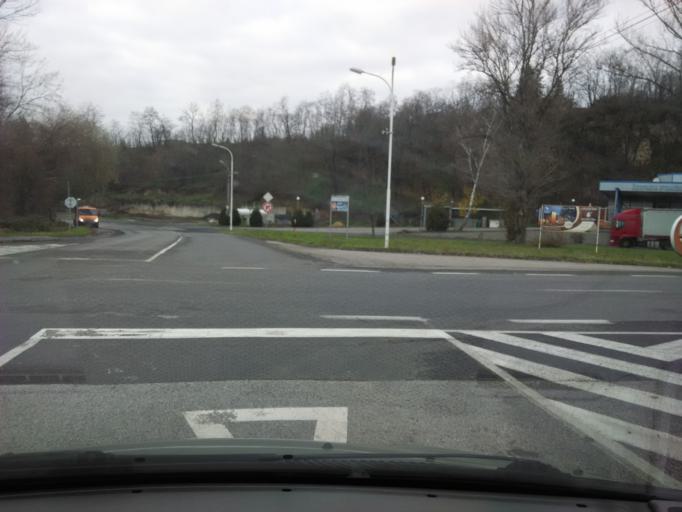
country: SK
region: Nitriansky
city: Tlmace
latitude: 48.2910
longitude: 18.5268
